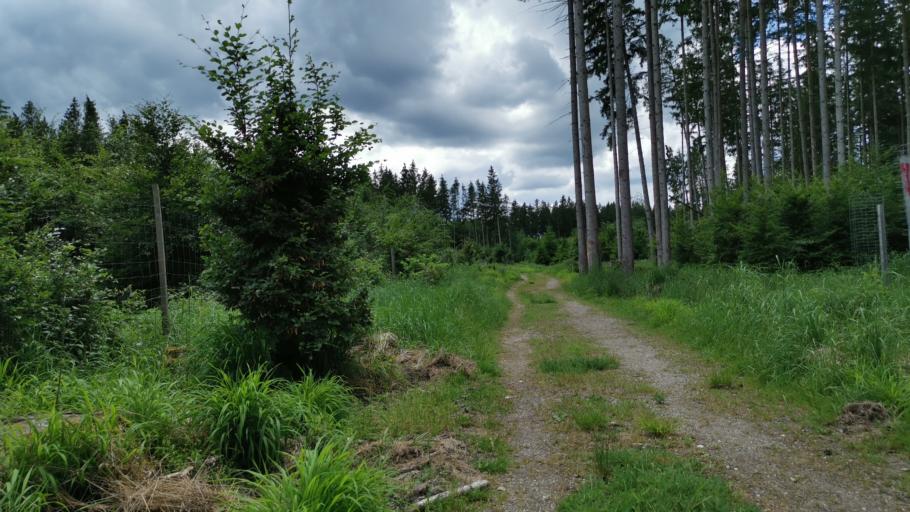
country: DE
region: Bavaria
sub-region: Upper Bavaria
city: Pullach im Isartal
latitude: 48.0561
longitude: 11.4967
